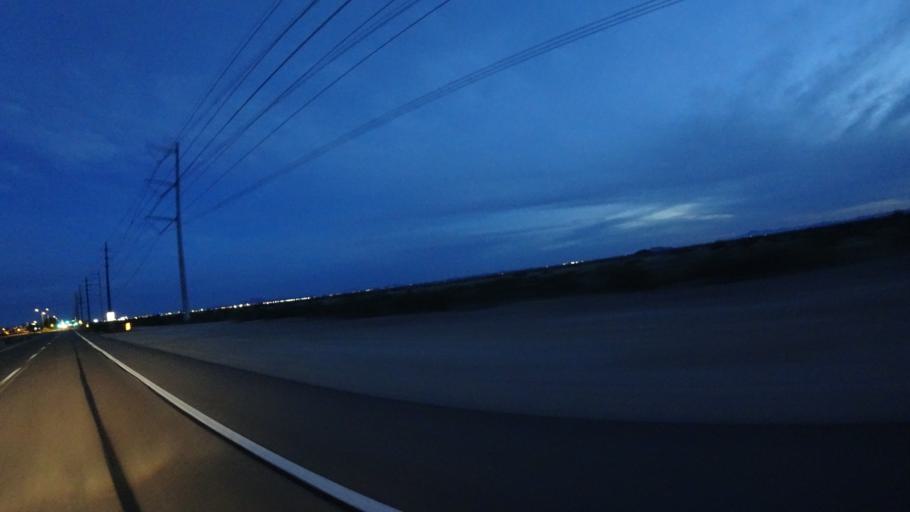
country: US
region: Arizona
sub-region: Maricopa County
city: Guadalupe
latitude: 33.2910
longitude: -112.0368
